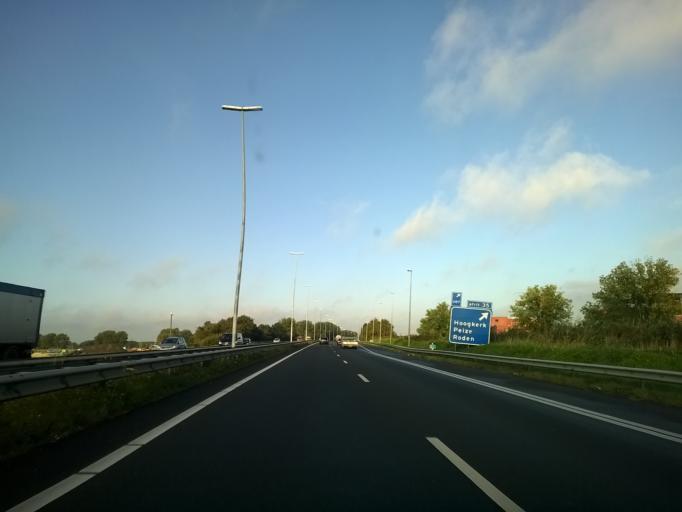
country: NL
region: Groningen
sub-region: Gemeente Groningen
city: Groningen
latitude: 53.1974
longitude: 6.5212
